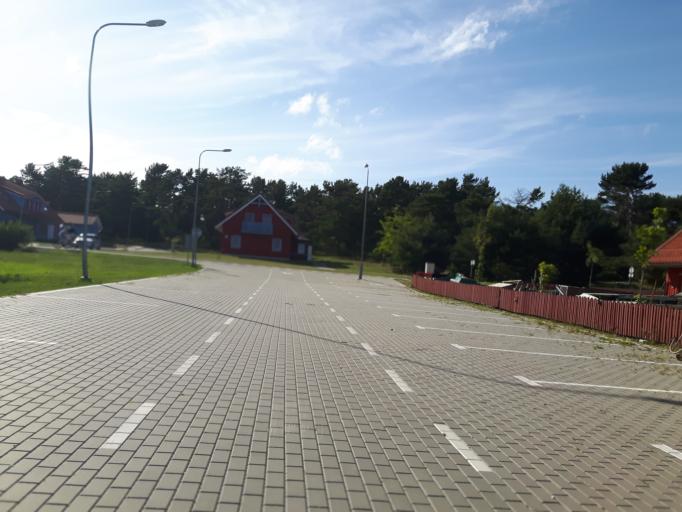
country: LT
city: Nida
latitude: 55.3179
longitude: 21.0211
